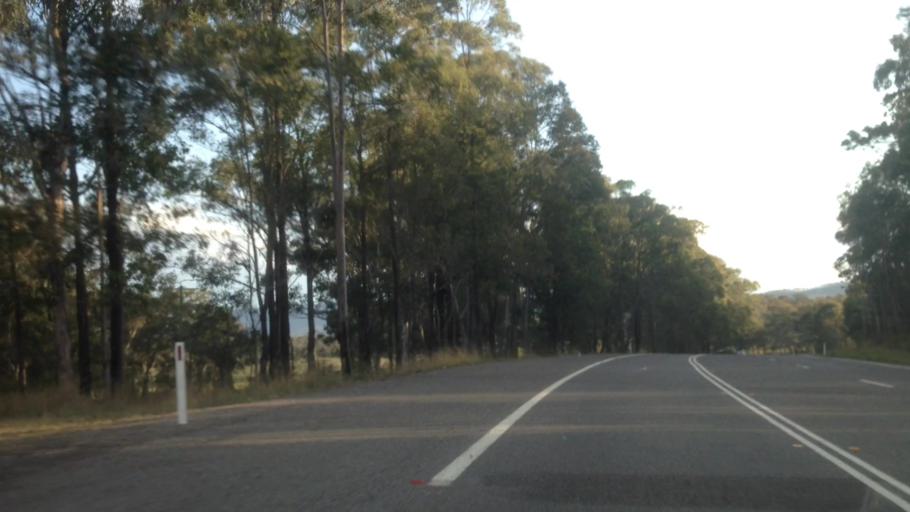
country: AU
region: New South Wales
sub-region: Cessnock
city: Kurri Kurri
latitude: -32.8606
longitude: 151.4836
